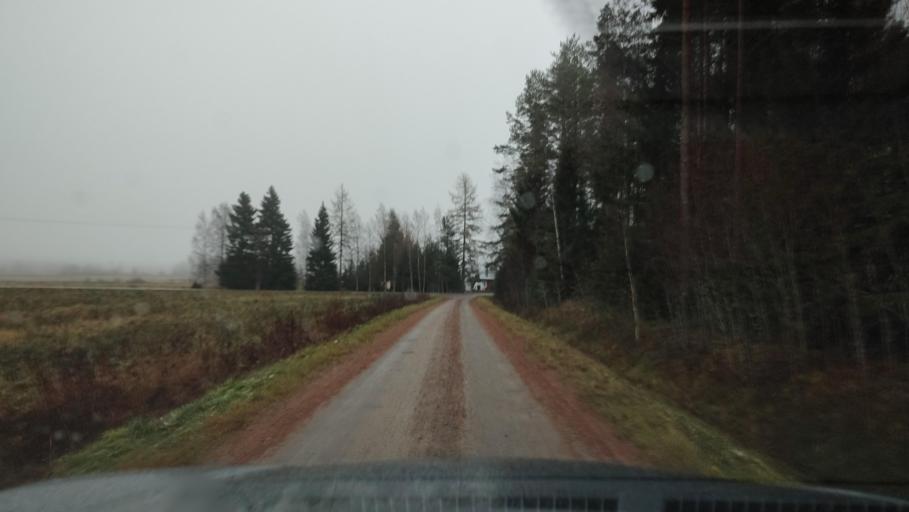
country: FI
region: Southern Ostrobothnia
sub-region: Suupohja
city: Karijoki
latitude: 62.1842
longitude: 21.7803
